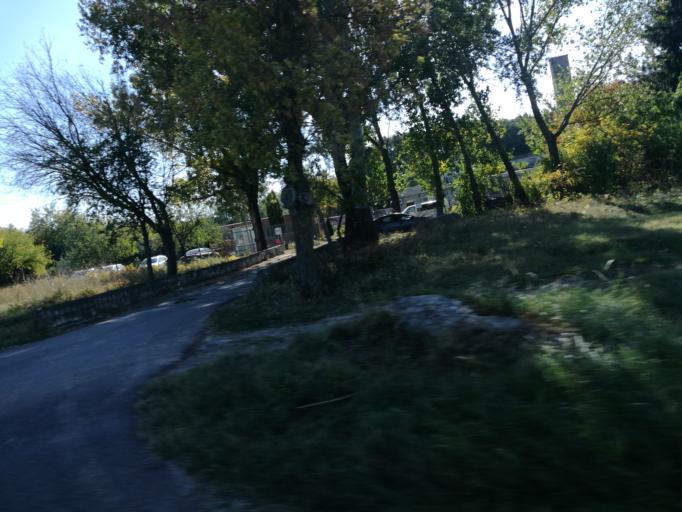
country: RO
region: Ilfov
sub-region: Comuna Dragomiresti-Vale
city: Dragomiresti-Vale
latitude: 44.4715
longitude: 25.9156
